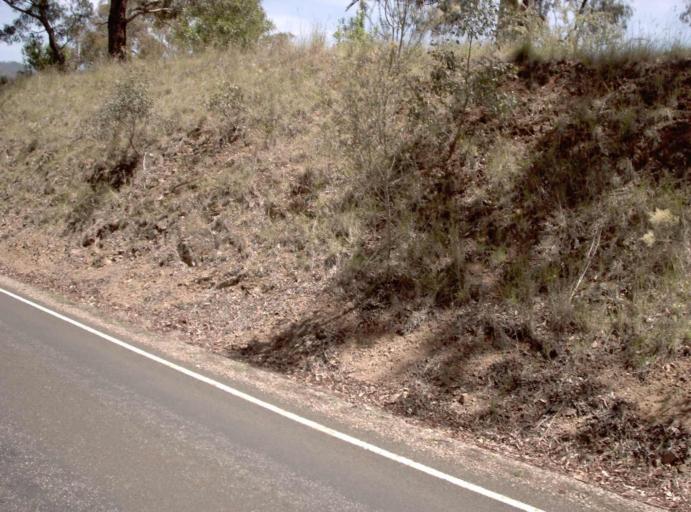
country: AU
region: Victoria
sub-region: East Gippsland
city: Bairnsdale
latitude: -37.3774
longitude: 147.8324
